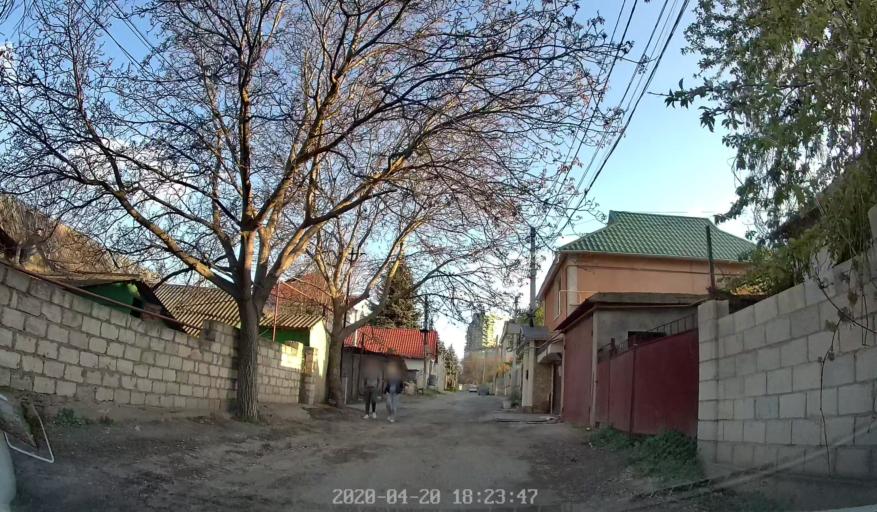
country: MD
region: Chisinau
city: Chisinau
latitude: 46.9951
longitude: 28.8377
